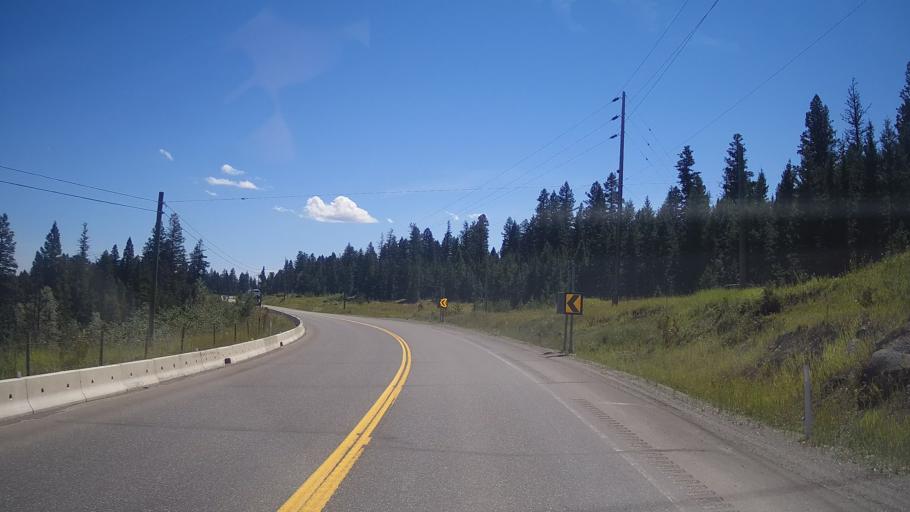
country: CA
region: British Columbia
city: Cache Creek
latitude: 51.1858
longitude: -121.5211
